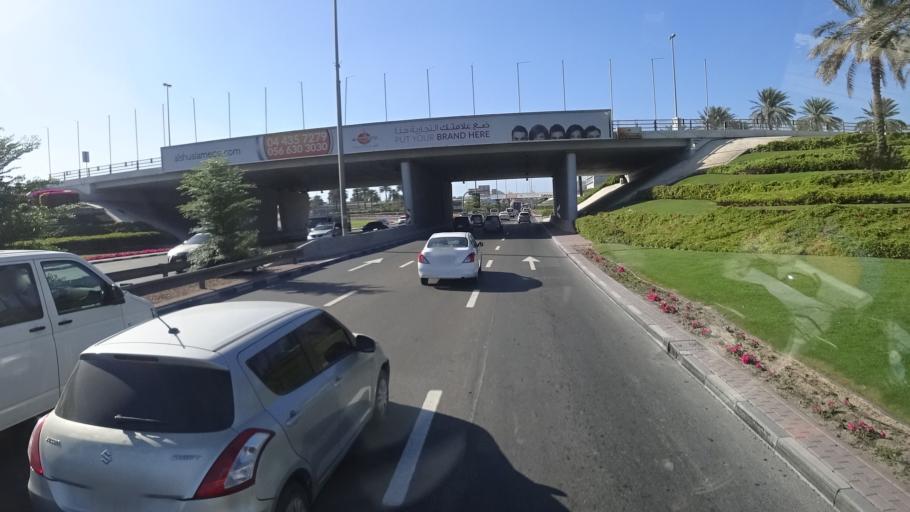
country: AE
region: Ash Shariqah
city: Sharjah
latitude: 25.2378
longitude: 55.3443
